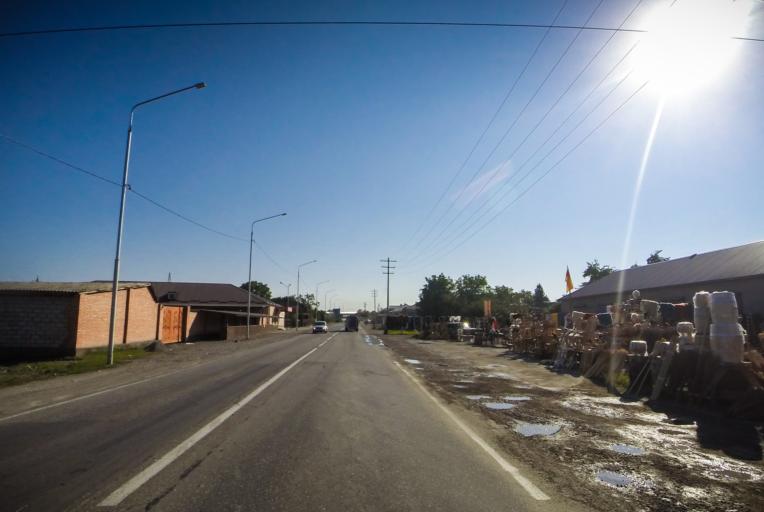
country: RU
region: North Ossetia
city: Arkhonskaya
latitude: 43.1158
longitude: 44.4961
